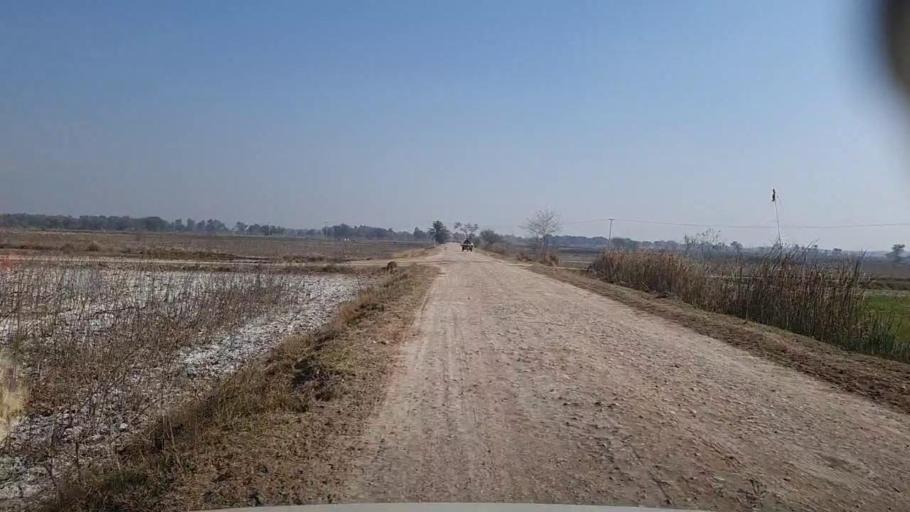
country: PK
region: Sindh
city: Khairpur
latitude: 27.9773
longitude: 69.7161
